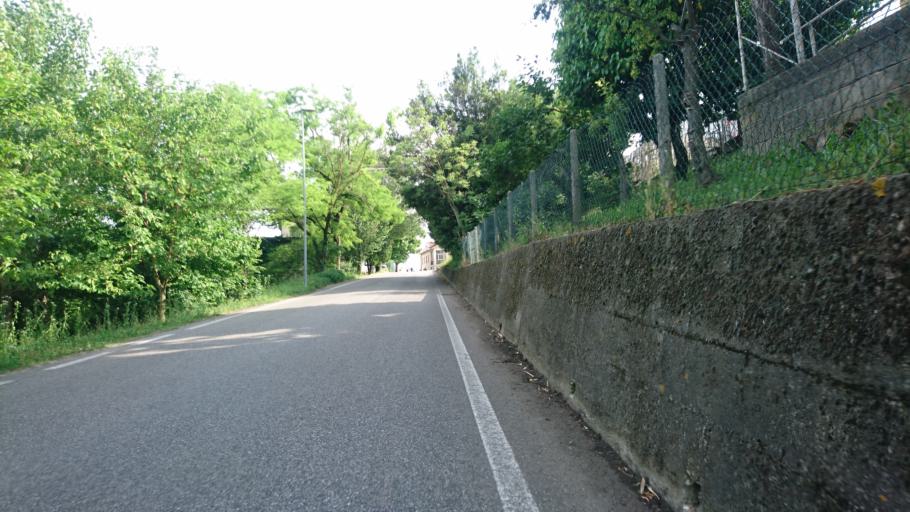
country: IT
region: Veneto
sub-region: Provincia di Treviso
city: Carpesica
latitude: 45.9510
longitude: 12.2912
